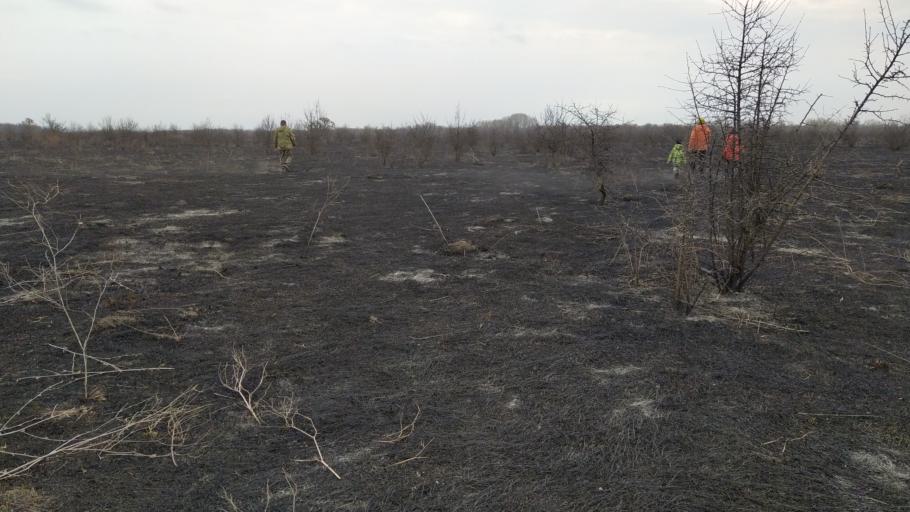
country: RU
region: Rostov
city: Semikarakorsk
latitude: 47.5473
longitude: 40.6823
